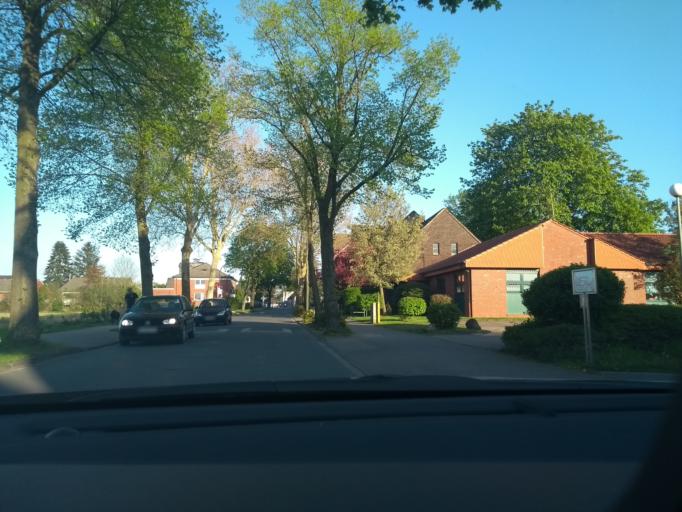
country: DE
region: North Rhine-Westphalia
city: Selm
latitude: 51.6666
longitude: 7.4609
